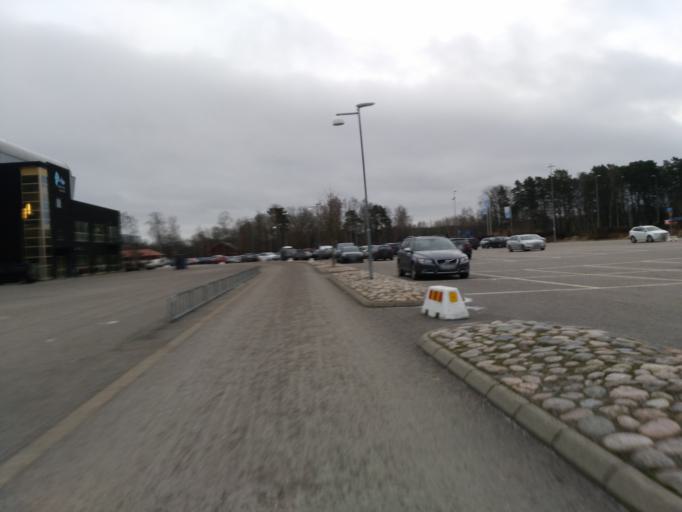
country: SE
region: Vaestra Goetaland
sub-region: Lidkopings Kommun
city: Lidkoping
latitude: 58.4939
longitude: 13.1416
